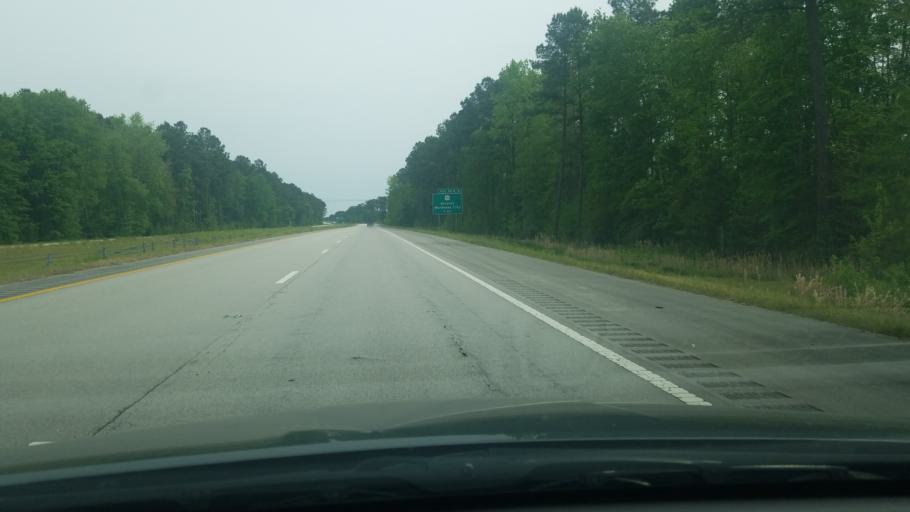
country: US
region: North Carolina
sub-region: Craven County
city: River Bend
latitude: 35.1170
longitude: -77.1580
